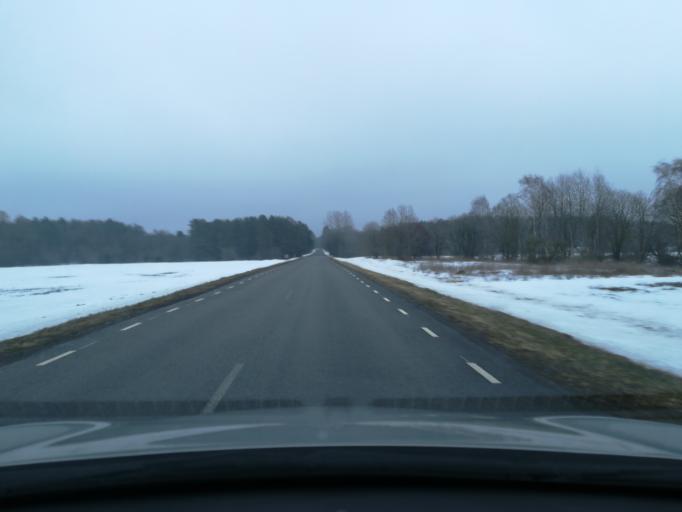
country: EE
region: Harju
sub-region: Kuusalu vald
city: Kuusalu
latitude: 59.4737
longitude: 25.5965
